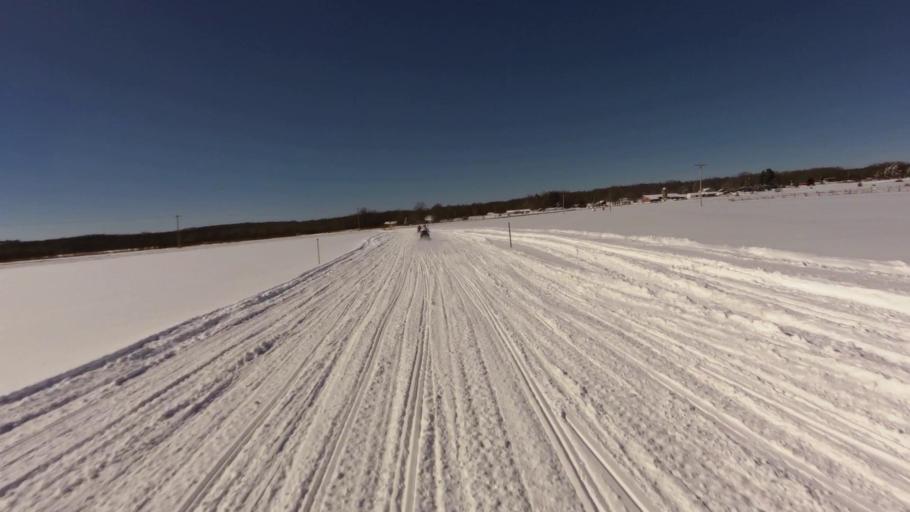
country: US
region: New York
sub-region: Chautauqua County
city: Mayville
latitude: 42.2724
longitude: -79.4827
